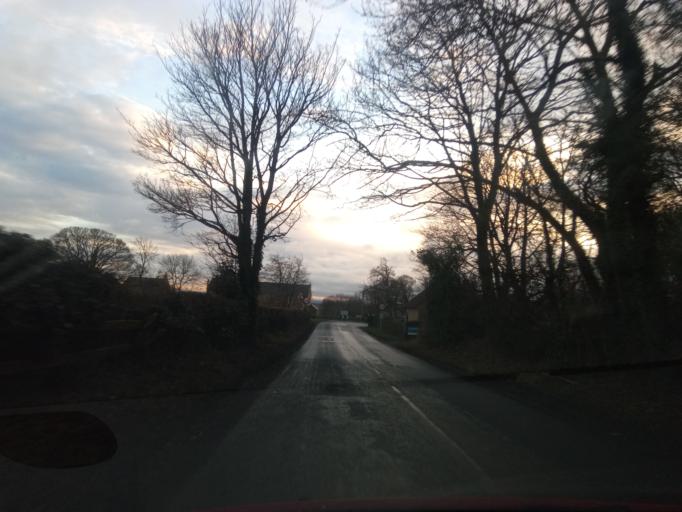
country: GB
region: England
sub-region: Northumberland
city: Meldon
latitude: 55.1280
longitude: -1.7920
